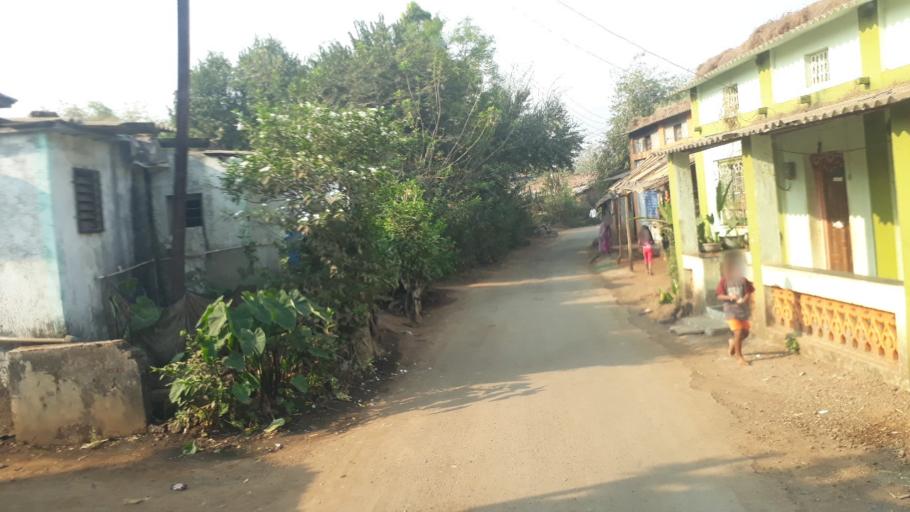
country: IN
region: Maharashtra
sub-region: Raigarh
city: Neral
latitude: 19.0458
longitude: 73.3301
